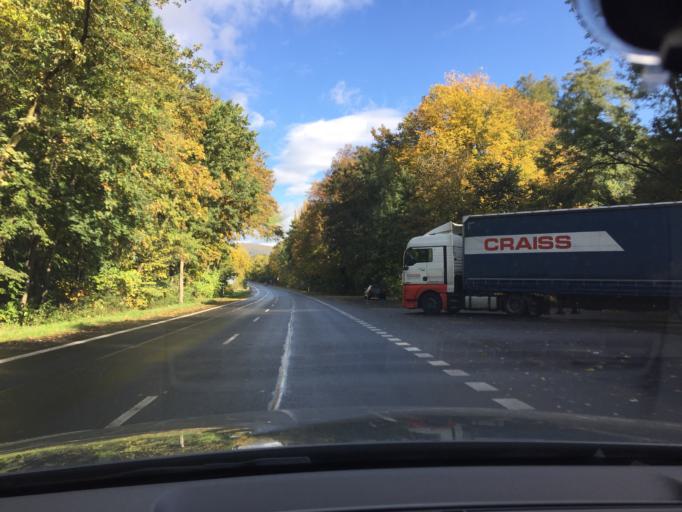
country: CZ
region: Ustecky
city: Chlumec
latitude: 50.6974
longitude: 13.9442
